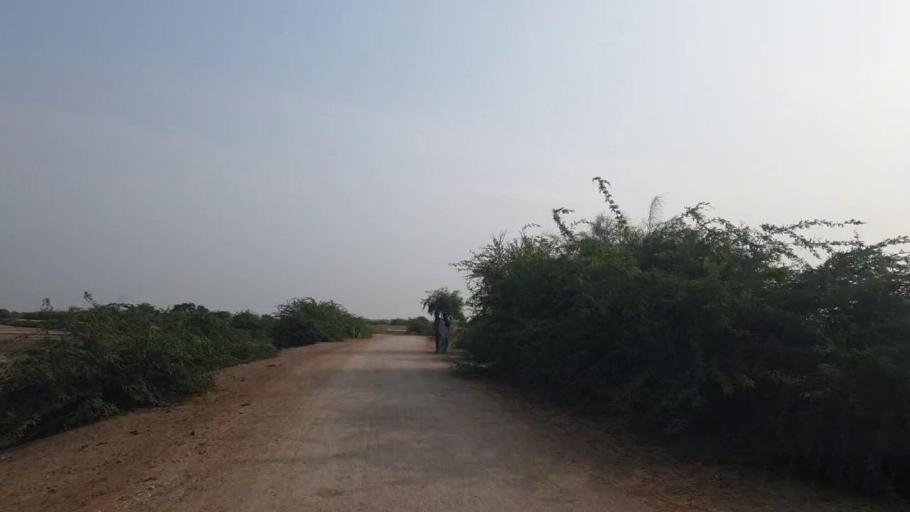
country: PK
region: Sindh
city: Badin
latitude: 24.6075
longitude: 68.6885
